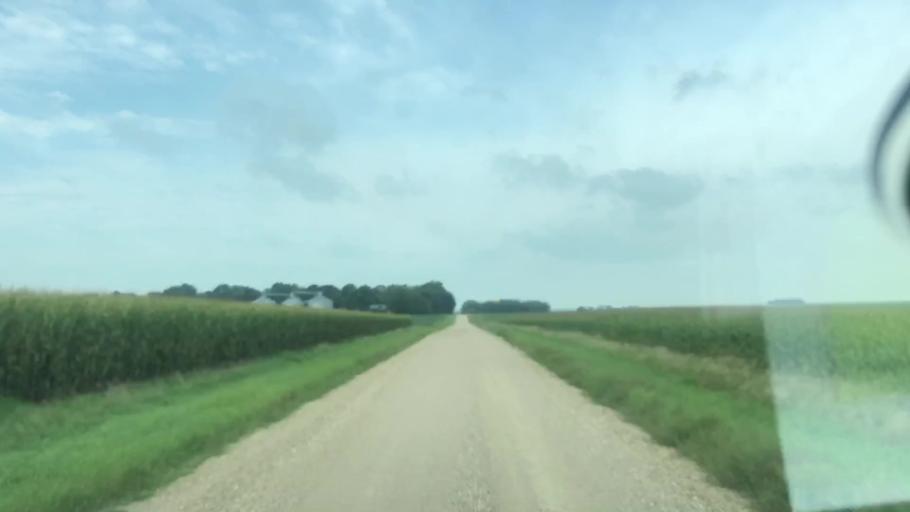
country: US
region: Iowa
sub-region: Lyon County
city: George
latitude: 43.2722
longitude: -95.9669
